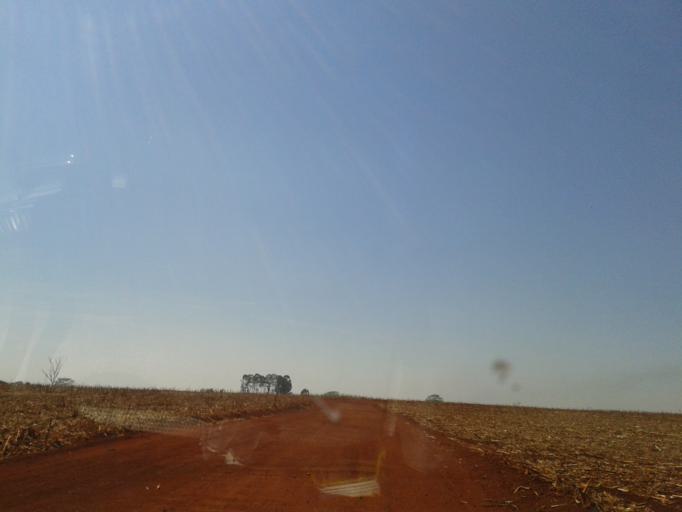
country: BR
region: Minas Gerais
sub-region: Capinopolis
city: Capinopolis
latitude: -18.5970
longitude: -49.5178
